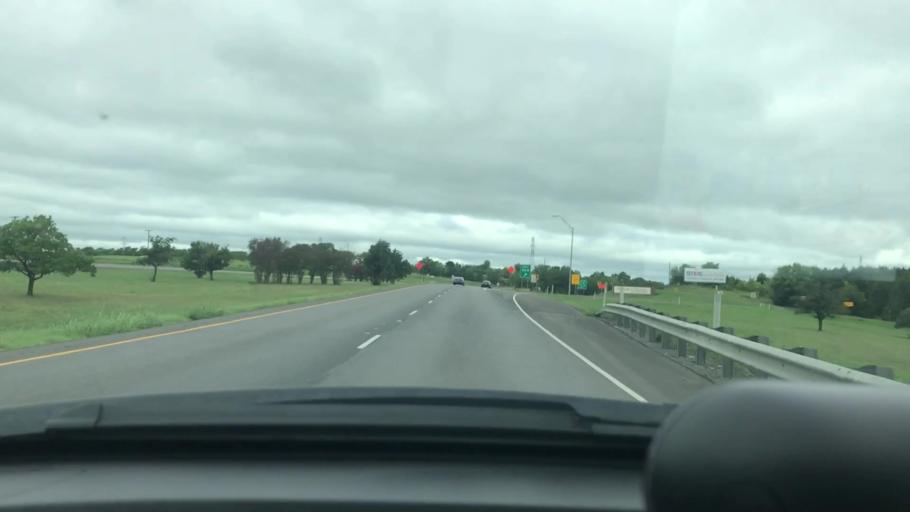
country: US
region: Texas
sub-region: Grayson County
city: Sherman
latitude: 33.6013
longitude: -96.6078
